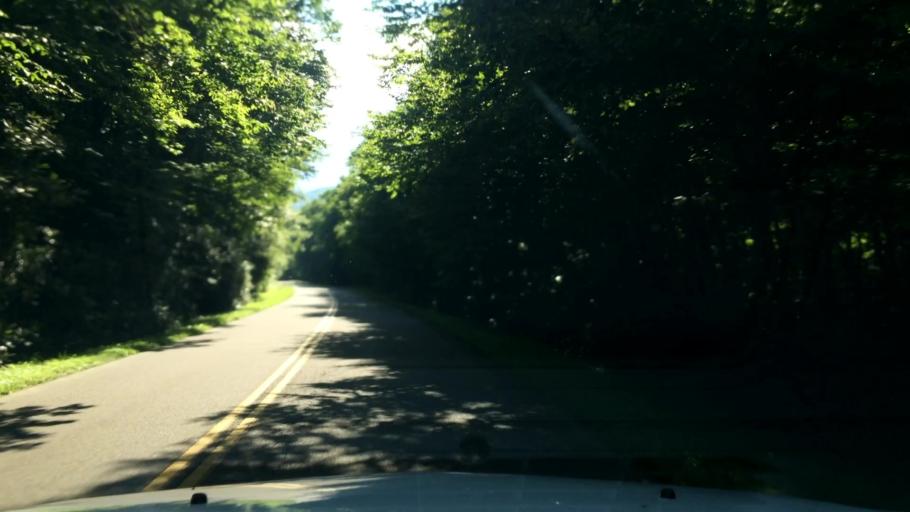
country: US
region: North Carolina
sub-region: Watauga County
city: Foscoe
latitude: 36.1321
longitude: -81.7586
